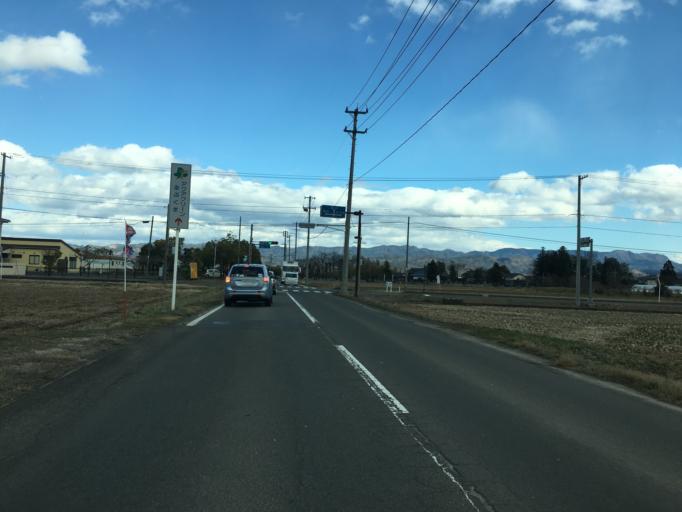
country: JP
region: Fukushima
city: Yanagawamachi-saiwaicho
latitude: 37.8678
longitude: 140.5638
